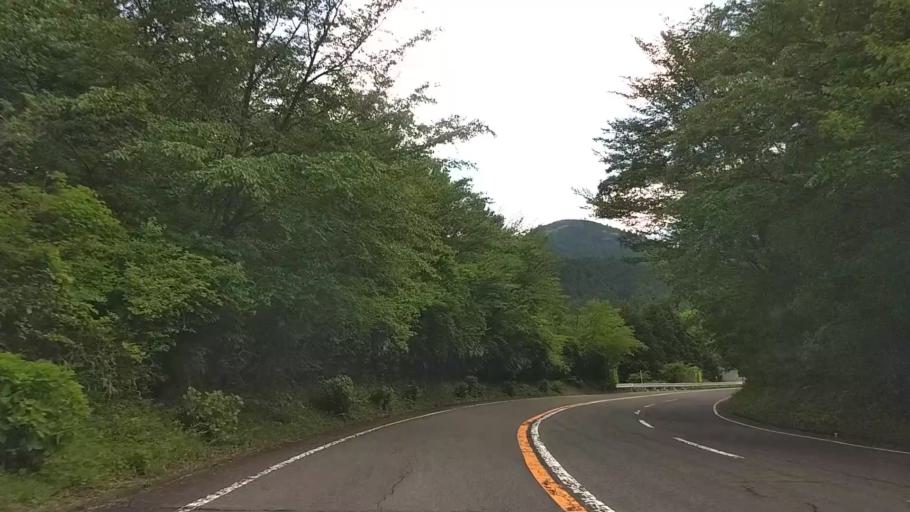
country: JP
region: Kanagawa
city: Odawara
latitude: 35.2153
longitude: 139.1018
